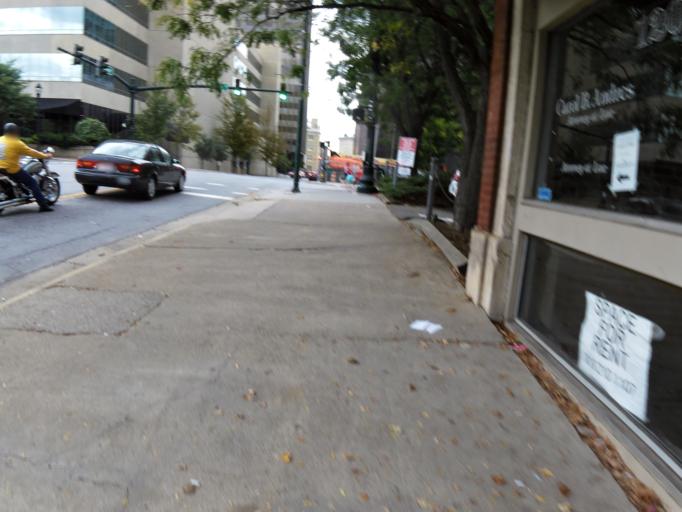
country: US
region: North Carolina
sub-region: Buncombe County
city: Asheville
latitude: 35.5959
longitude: -82.5505
